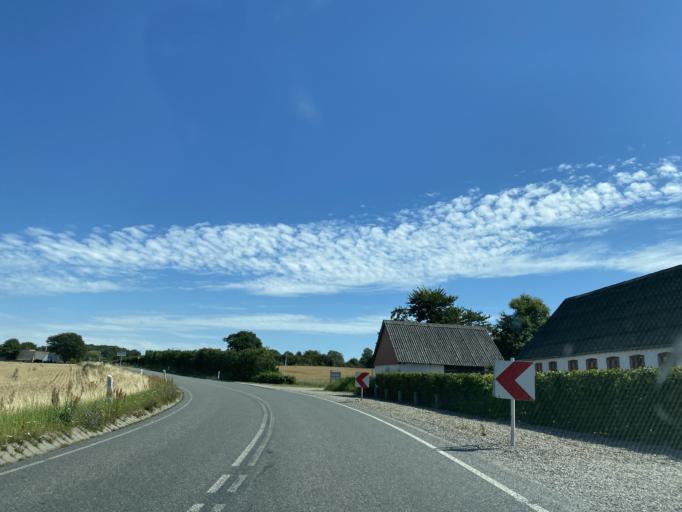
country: DK
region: South Denmark
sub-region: Faaborg-Midtfyn Kommune
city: Ringe
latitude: 55.2077
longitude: 10.3818
